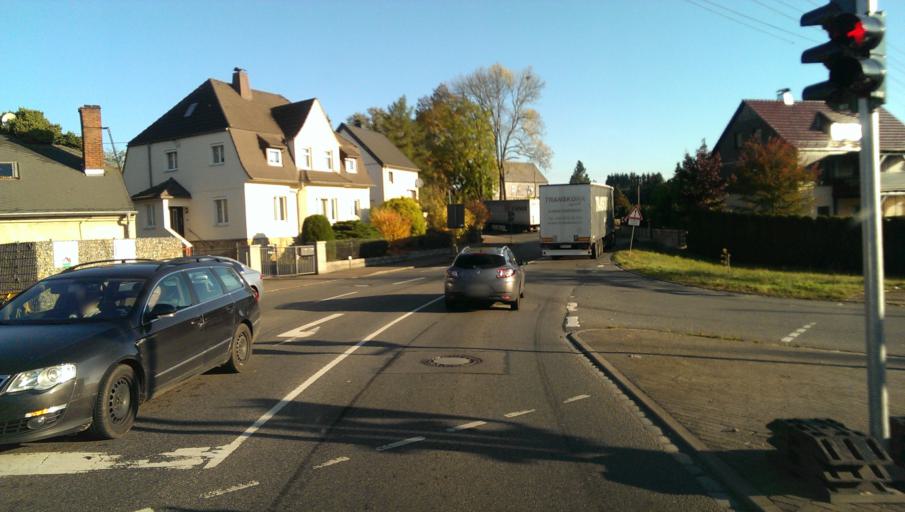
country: DE
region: Saxony
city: Hilbersdorf
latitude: 50.9051
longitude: 12.9786
